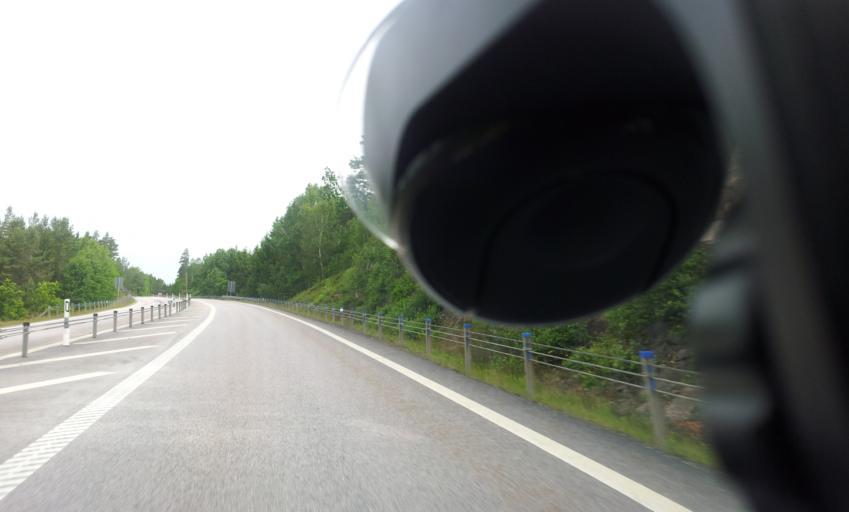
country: SE
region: Kalmar
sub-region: Vasterviks Kommun
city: Forserum
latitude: 58.0234
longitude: 16.5191
